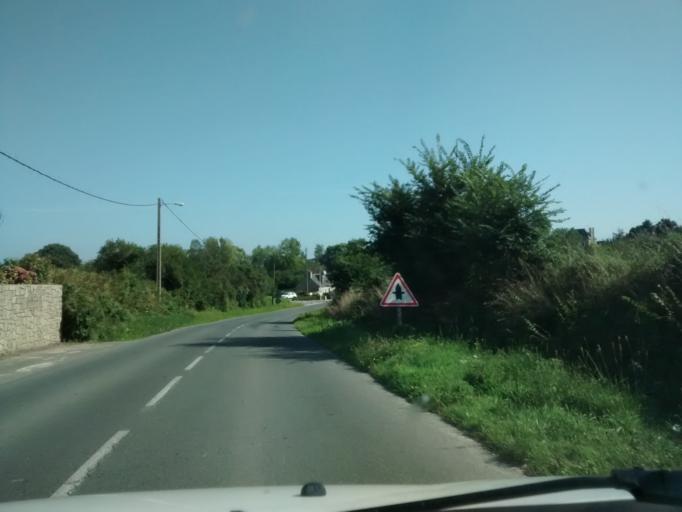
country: FR
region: Brittany
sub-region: Departement des Cotes-d'Armor
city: Pleubian
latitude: 48.8510
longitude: -3.1282
